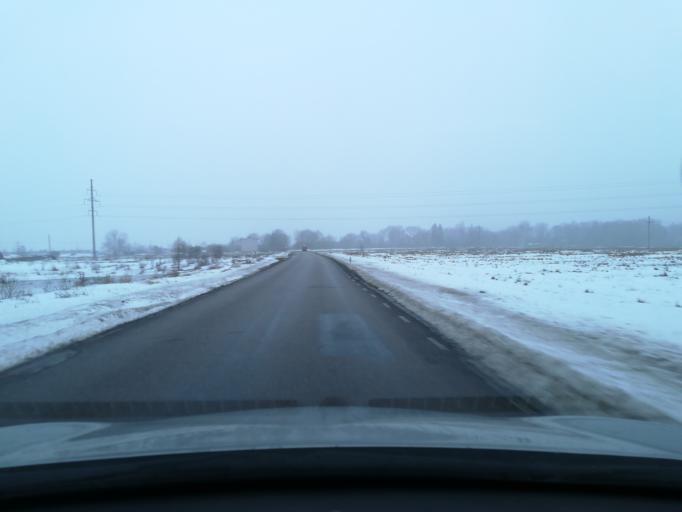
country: EE
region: Harju
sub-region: Rae vald
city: Jueri
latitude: 59.3771
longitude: 24.8946
